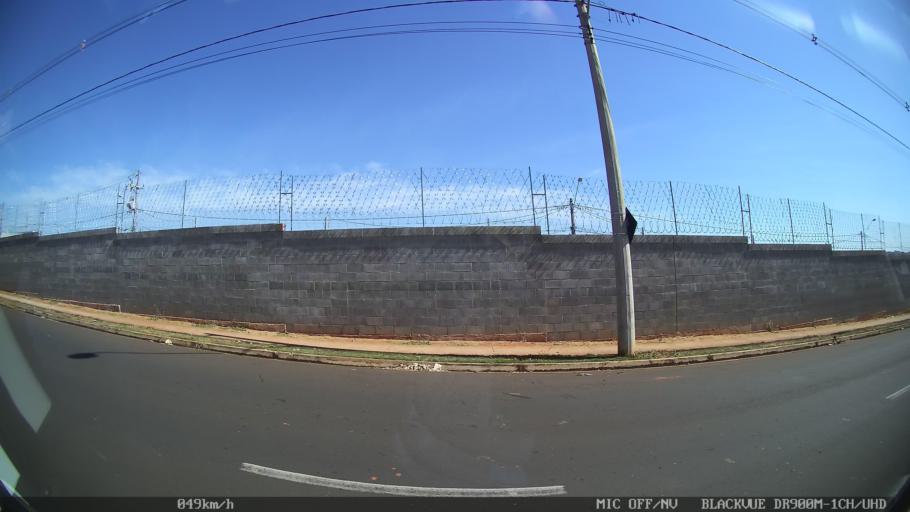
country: BR
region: Sao Paulo
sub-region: Sao Jose Do Rio Preto
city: Sao Jose do Rio Preto
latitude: -20.7639
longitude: -49.4200
